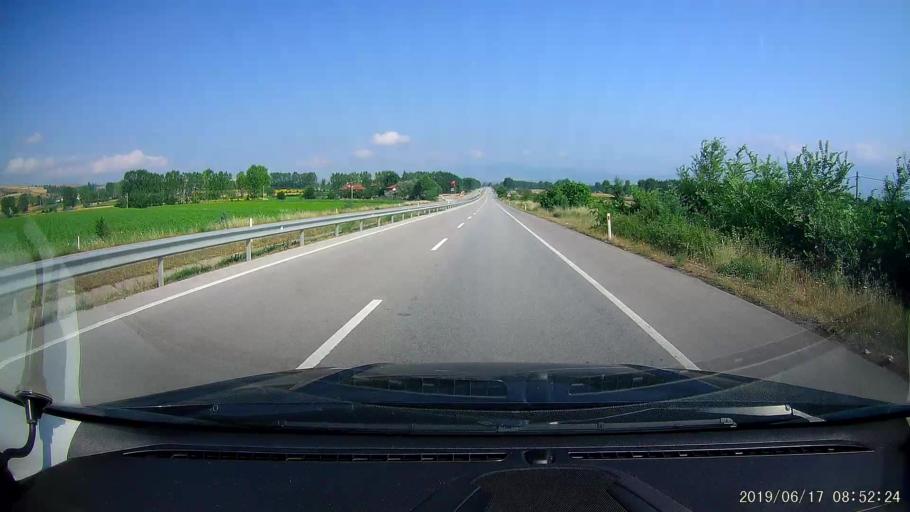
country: TR
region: Tokat
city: Erbaa
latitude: 40.6970
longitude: 36.4974
